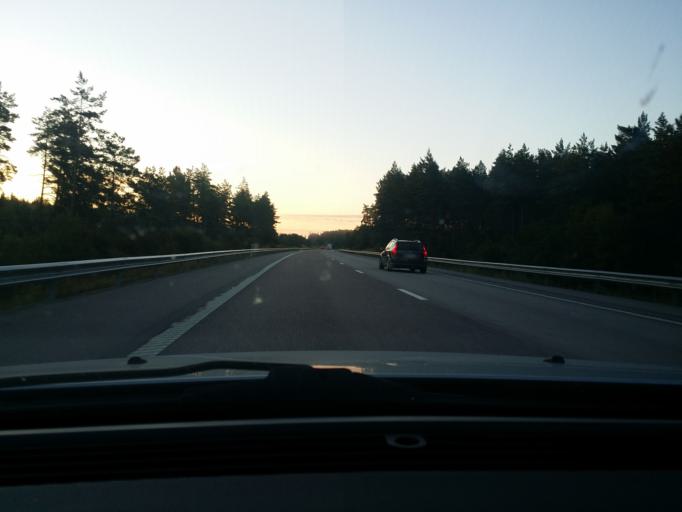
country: SE
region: Uppsala
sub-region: Enkopings Kommun
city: Grillby
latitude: 59.6435
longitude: 17.2016
